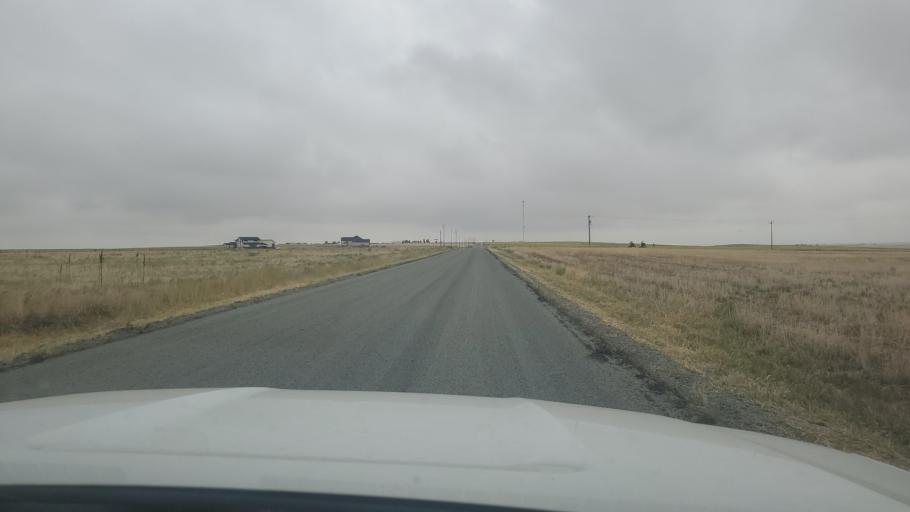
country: US
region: Colorado
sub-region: Weld County
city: Lochbuie
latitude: 39.9302
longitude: -104.6028
